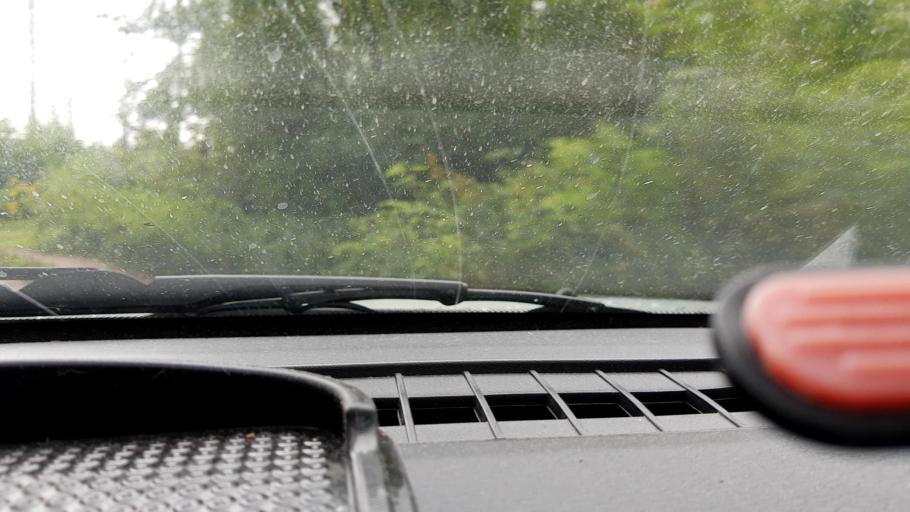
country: RU
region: Nizjnij Novgorod
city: Afonino
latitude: 56.3236
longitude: 44.1603
